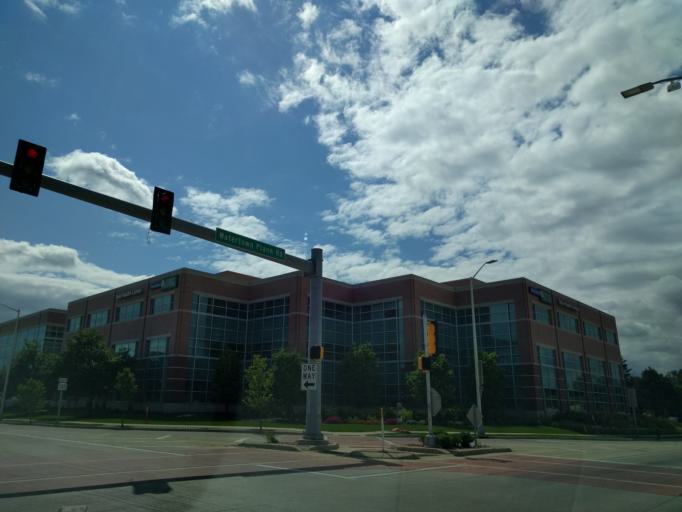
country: US
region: Wisconsin
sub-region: Waukesha County
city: Elm Grove
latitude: 43.0455
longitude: -88.0473
